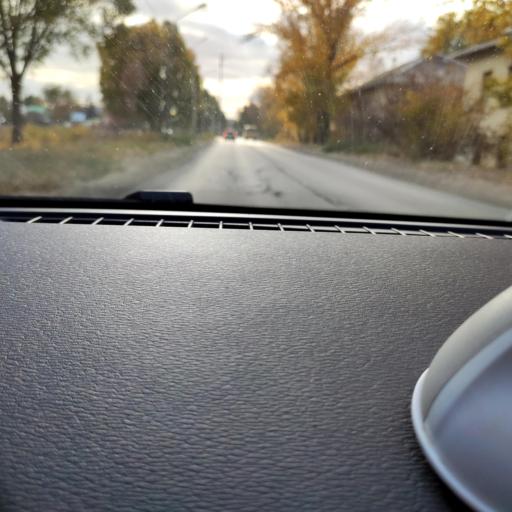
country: RU
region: Samara
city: Petra-Dubrava
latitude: 53.2395
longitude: 50.3078
